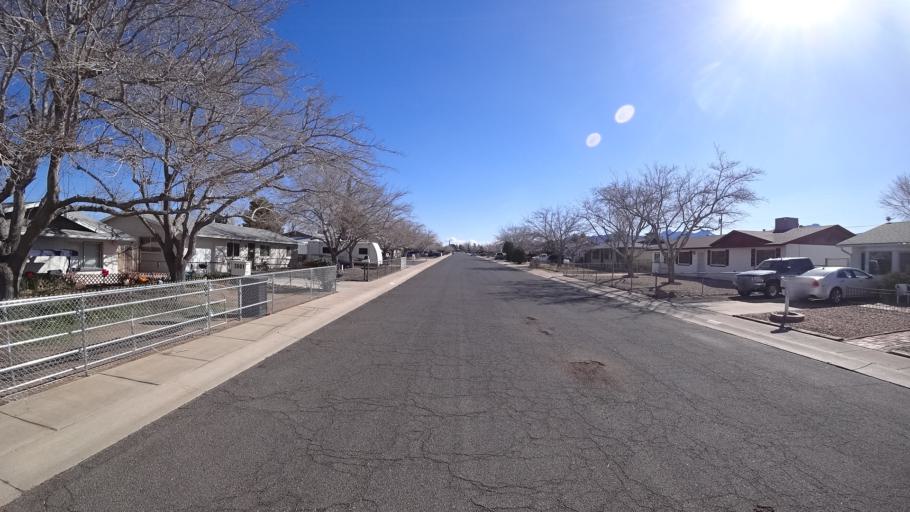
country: US
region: Arizona
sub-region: Mohave County
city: Kingman
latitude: 35.1949
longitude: -114.0176
